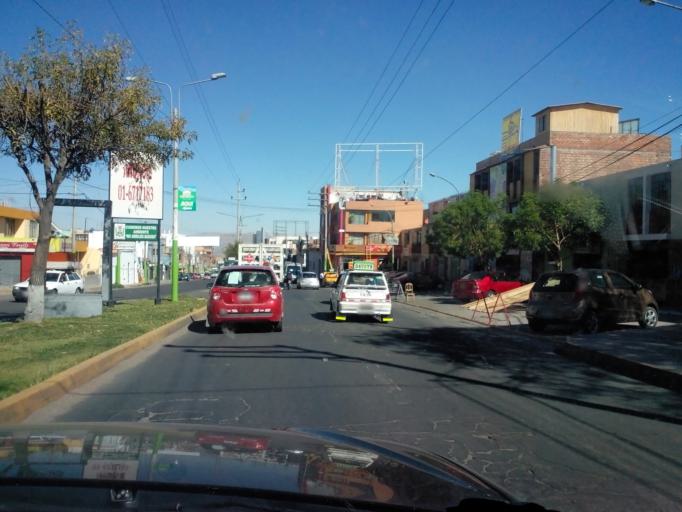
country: PE
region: Arequipa
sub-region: Provincia de Arequipa
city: Arequipa
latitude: -16.3774
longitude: -71.5571
